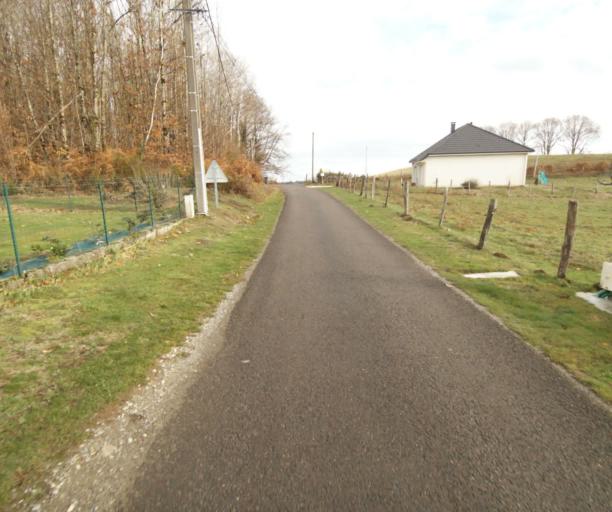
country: FR
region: Limousin
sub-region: Departement de la Correze
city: Saint-Mexant
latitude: 45.2801
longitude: 1.6474
